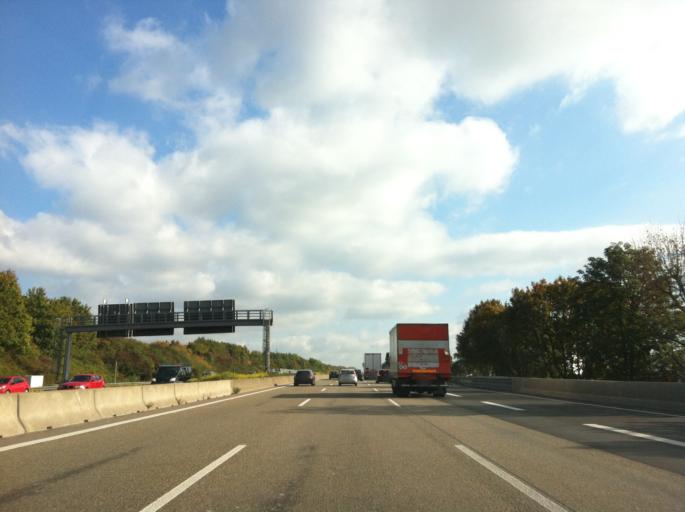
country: DE
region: North Rhine-Westphalia
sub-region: Regierungsbezirk Koln
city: Frechen
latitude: 50.9226
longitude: 6.8551
